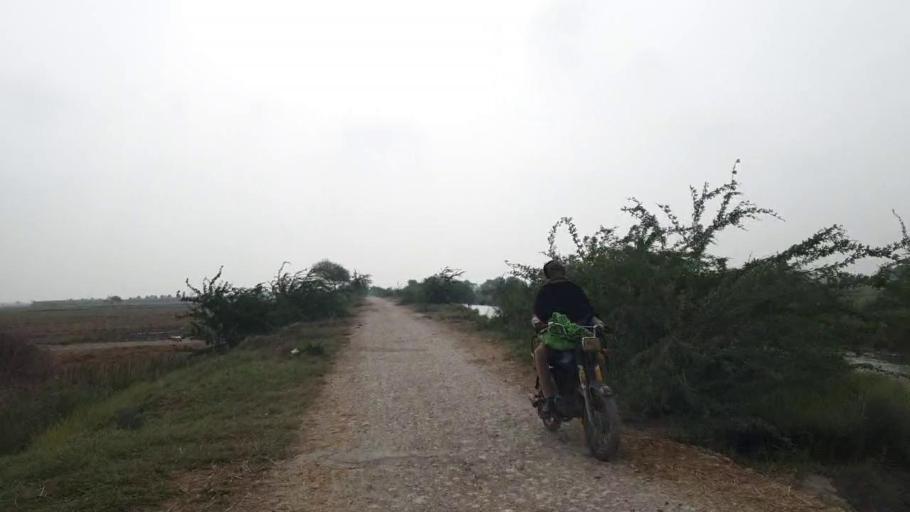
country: PK
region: Sindh
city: Kario
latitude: 24.8555
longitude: 68.5267
